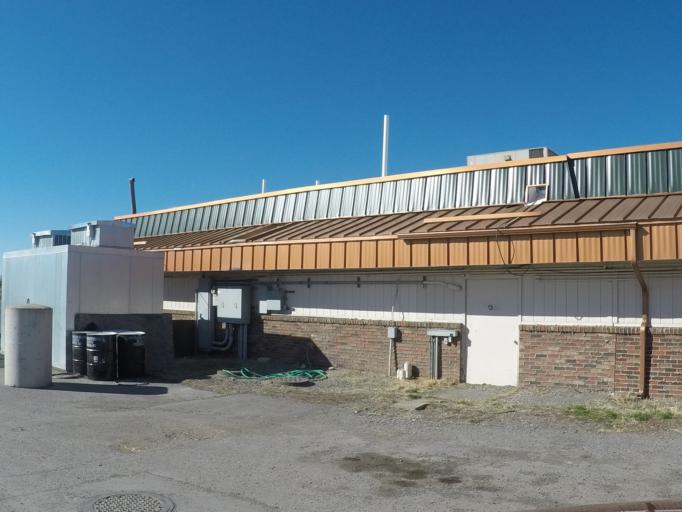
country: US
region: Montana
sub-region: Sweet Grass County
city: Big Timber
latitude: 45.8269
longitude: -109.9719
